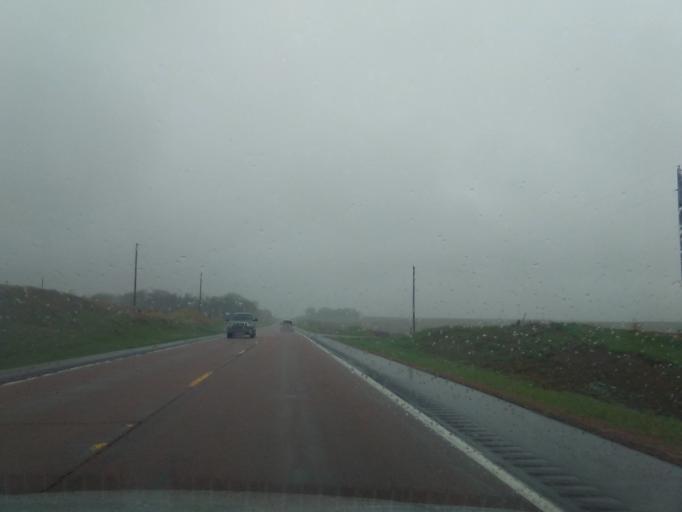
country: US
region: Nebraska
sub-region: Wayne County
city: Wayne
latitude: 42.2355
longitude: -97.1434
